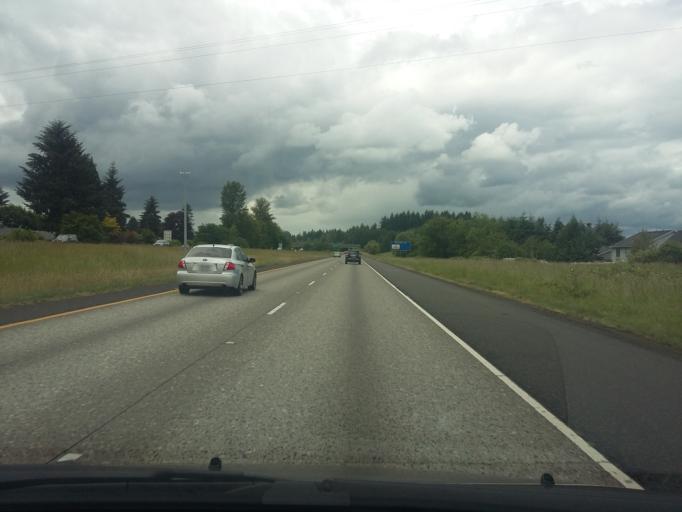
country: US
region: Washington
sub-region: Clark County
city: Five Corners
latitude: 45.6731
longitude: -122.5827
